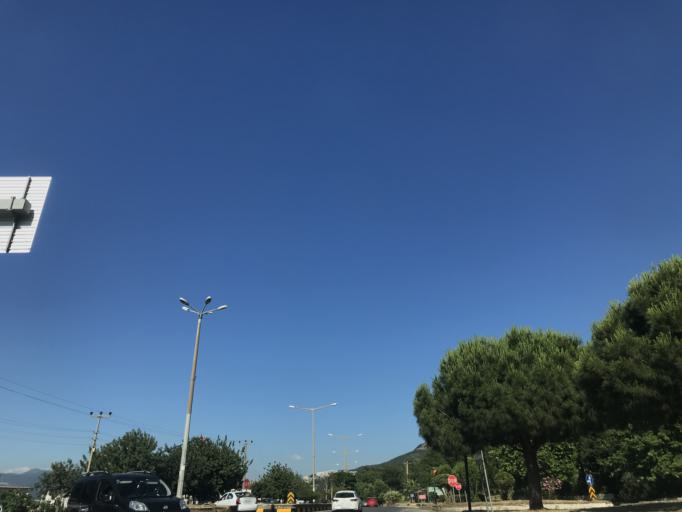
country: TR
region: Aydin
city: Davutlar
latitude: 37.7157
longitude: 27.2317
